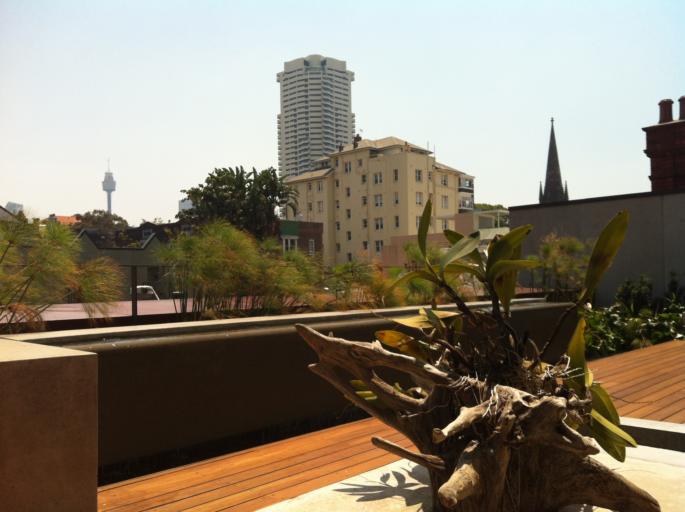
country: AU
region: New South Wales
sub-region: City of Sydney
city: Darlinghurst
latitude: -33.8787
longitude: 151.2215
